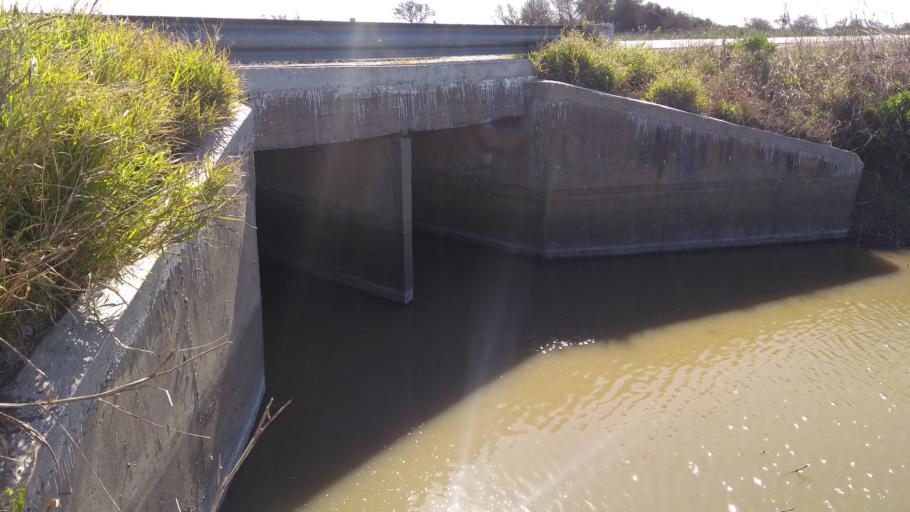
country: AR
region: Santiago del Estero
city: Los Juries
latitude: -28.6107
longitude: -61.5189
